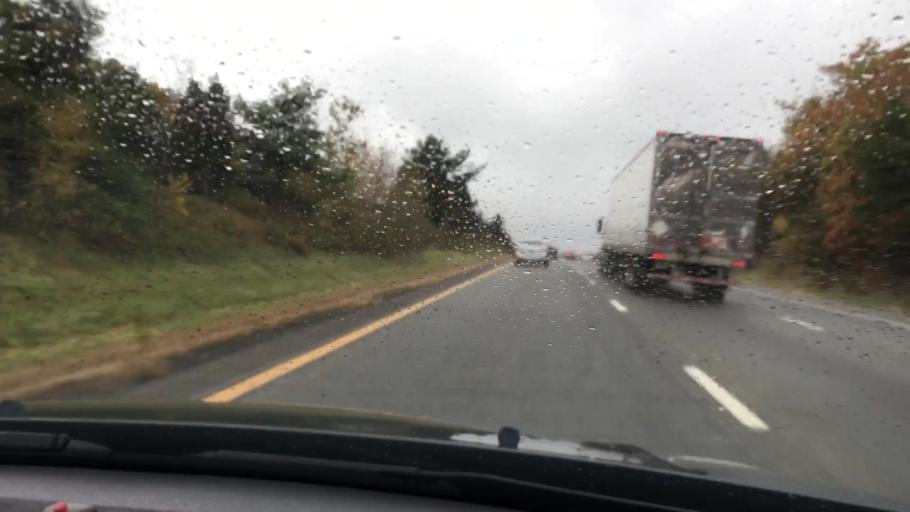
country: US
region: Massachusetts
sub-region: Middlesex County
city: Littleton Common
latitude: 42.5520
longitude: -71.4676
